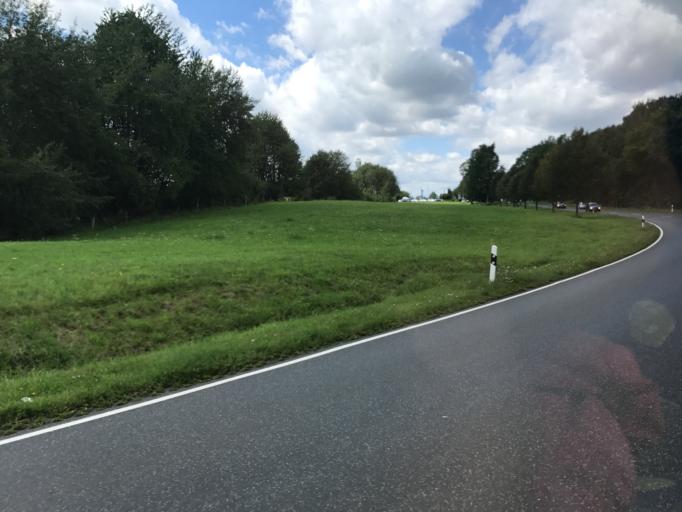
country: DE
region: Hesse
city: Weilburg
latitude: 50.4832
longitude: 8.2946
